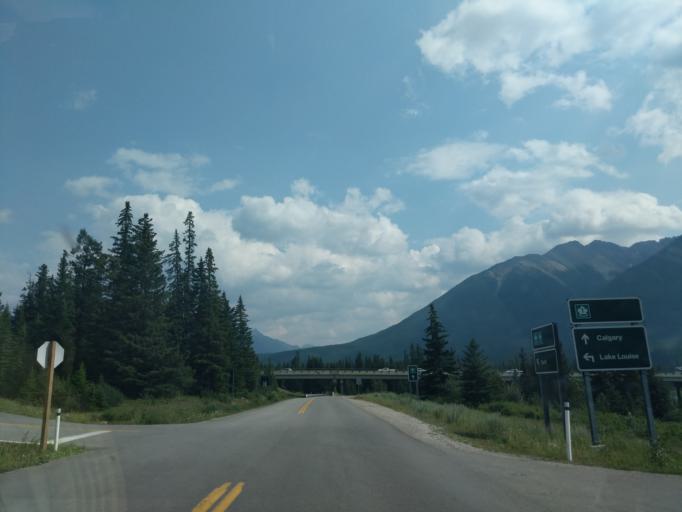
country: CA
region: Alberta
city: Banff
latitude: 51.1703
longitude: -115.6595
